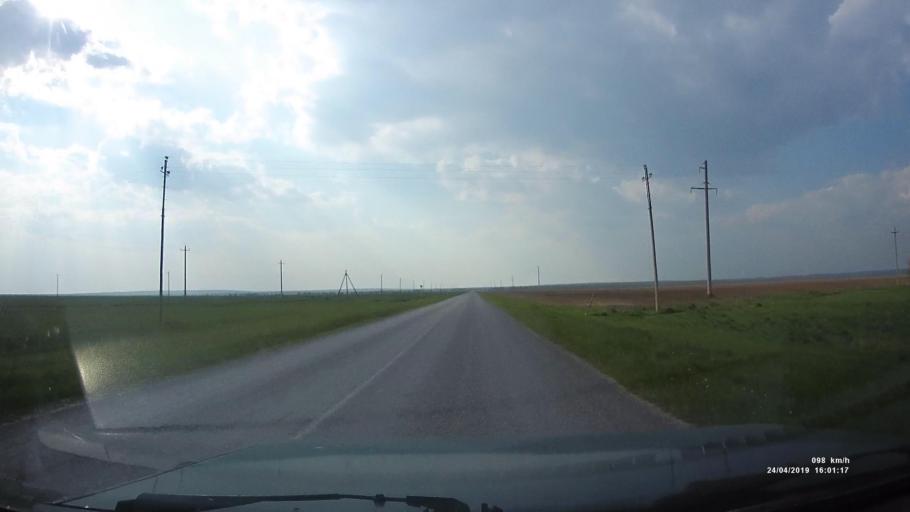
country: RU
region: Rostov
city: Sovetskoye
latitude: 46.6404
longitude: 42.4386
